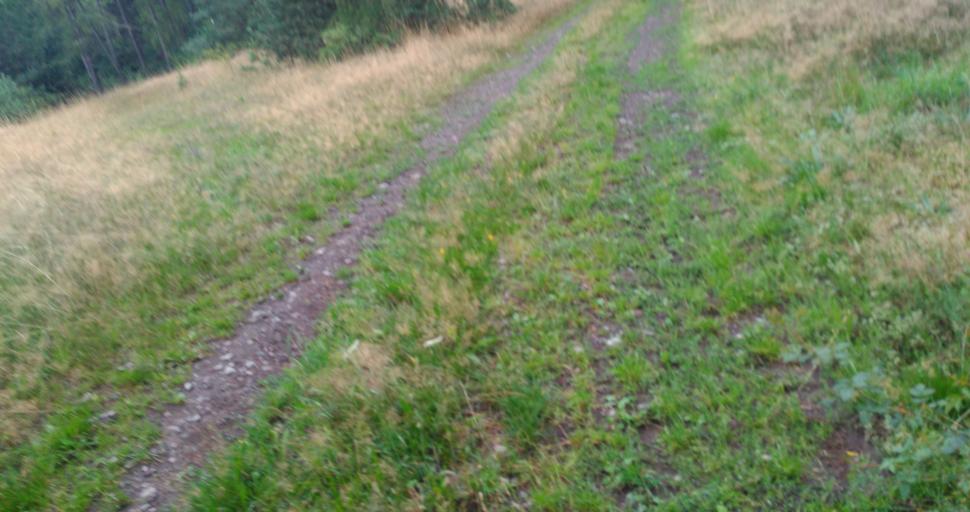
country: CZ
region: Central Bohemia
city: Jince
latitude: 49.7795
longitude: 13.9655
